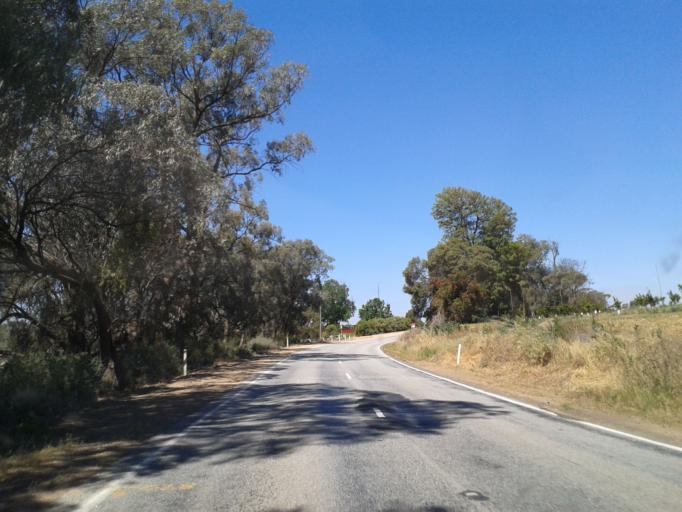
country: AU
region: Victoria
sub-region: Swan Hill
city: Swan Hill
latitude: -34.7210
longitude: 143.1714
